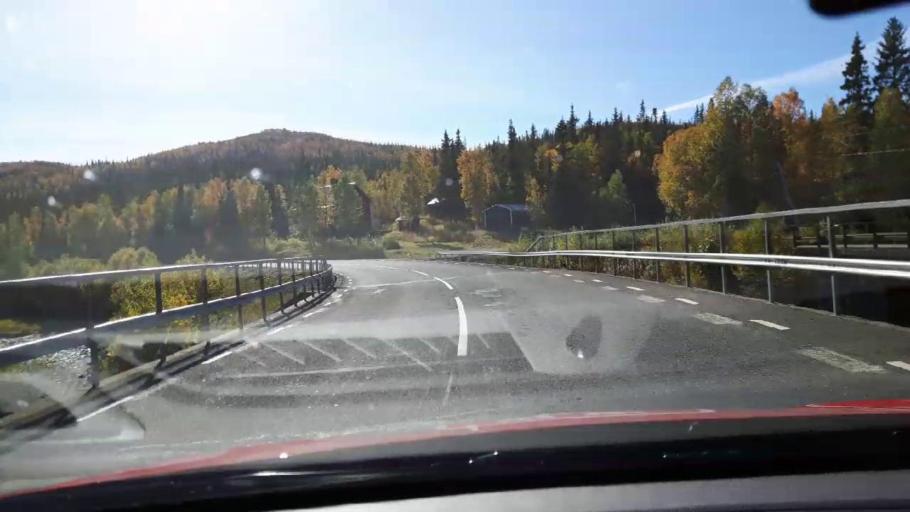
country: NO
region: Nord-Trondelag
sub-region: Royrvik
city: Royrvik
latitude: 64.8219
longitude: 14.0614
